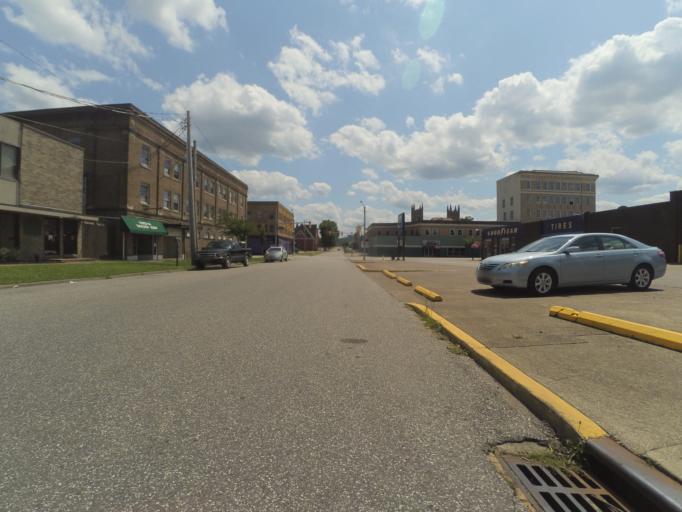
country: US
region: West Virginia
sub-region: Cabell County
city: Huntington
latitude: 38.4222
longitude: -82.4389
